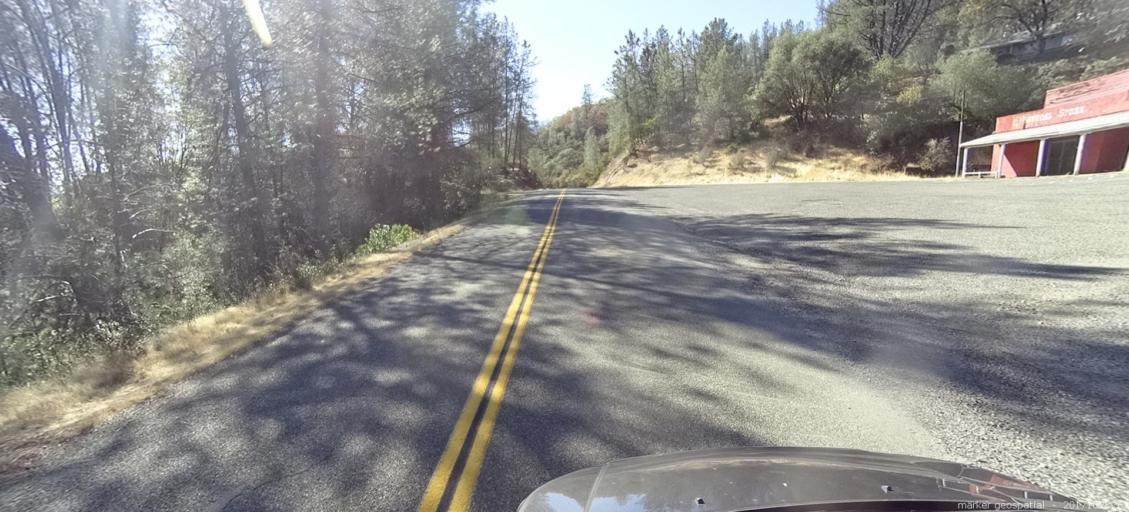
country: US
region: California
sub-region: Shasta County
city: Shasta
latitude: 40.6393
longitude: -122.5591
